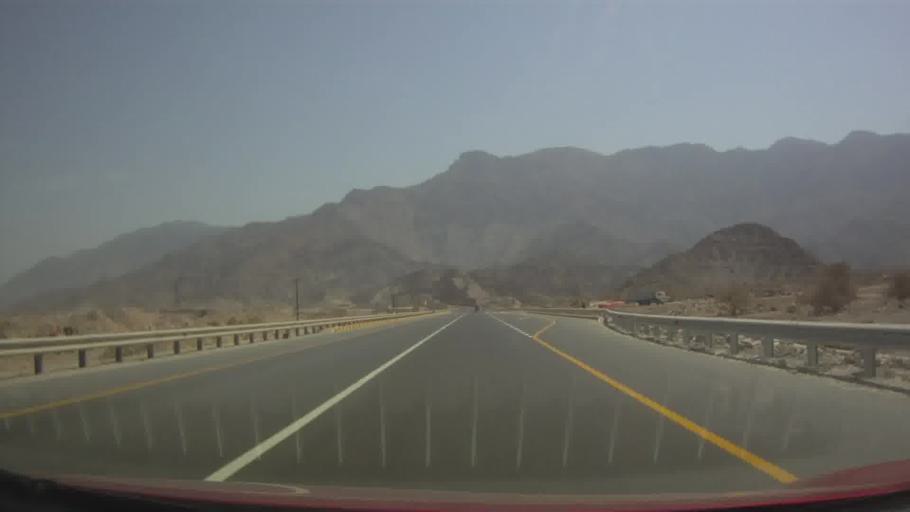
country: OM
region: Muhafazat Masqat
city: Muscat
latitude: 23.4060
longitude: 58.7802
